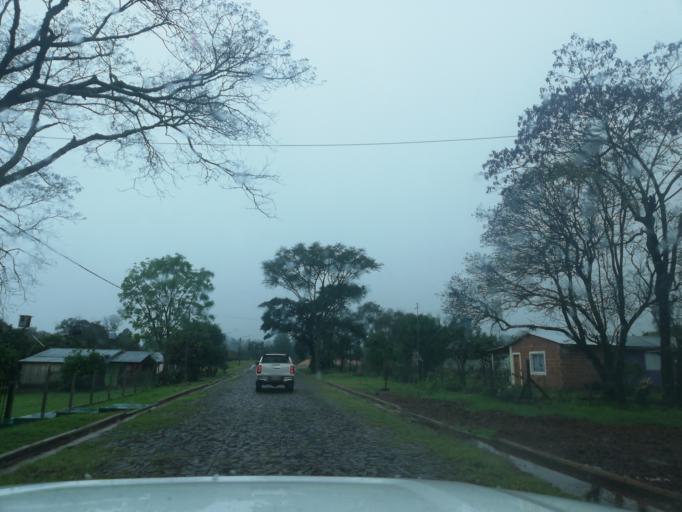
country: AR
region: Misiones
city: Almafuerte
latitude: -27.5077
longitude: -55.4015
